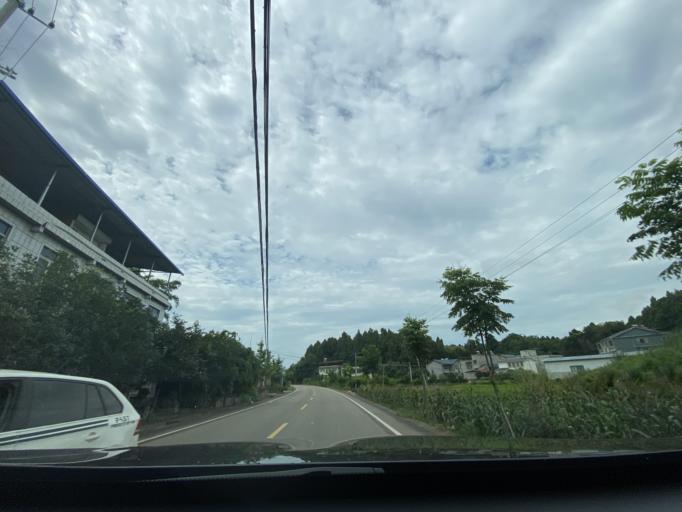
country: CN
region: Sichuan
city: Jiancheng
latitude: 30.4692
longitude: 104.6293
